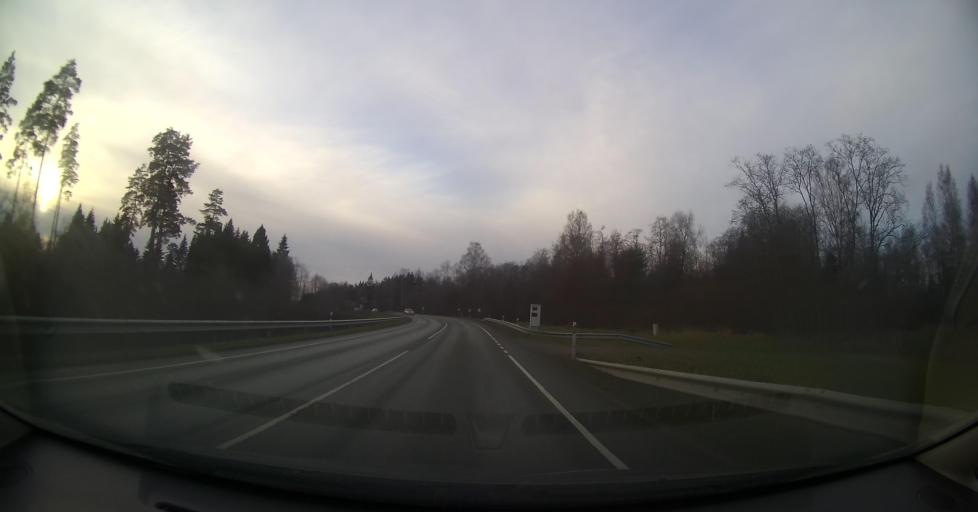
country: EE
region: Ida-Virumaa
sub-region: Toila vald
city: Voka
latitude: 59.3801
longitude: 27.5559
